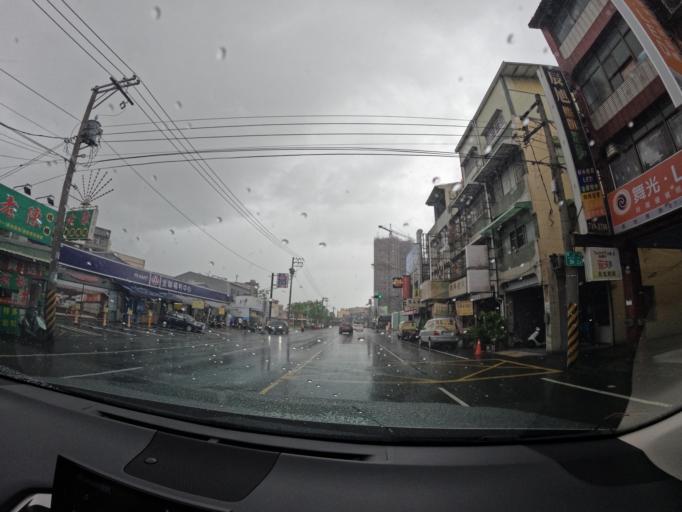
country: TW
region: Taiwan
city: Fengshan
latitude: 22.6400
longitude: 120.3645
